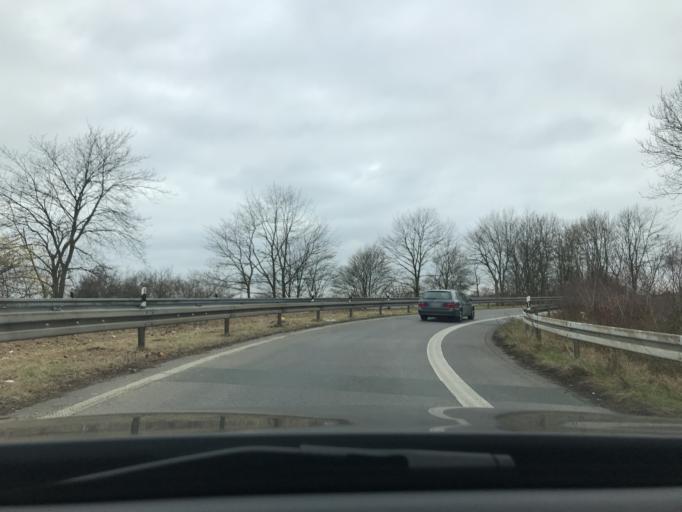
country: DE
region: North Rhine-Westphalia
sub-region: Regierungsbezirk Dusseldorf
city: Krefeld
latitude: 51.2855
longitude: 6.6056
